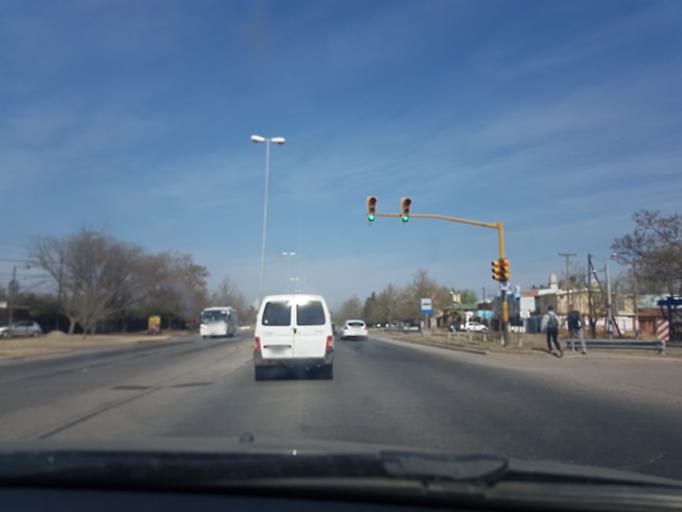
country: AR
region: Cordoba
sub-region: Departamento de Capital
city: Cordoba
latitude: -31.4818
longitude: -64.2420
